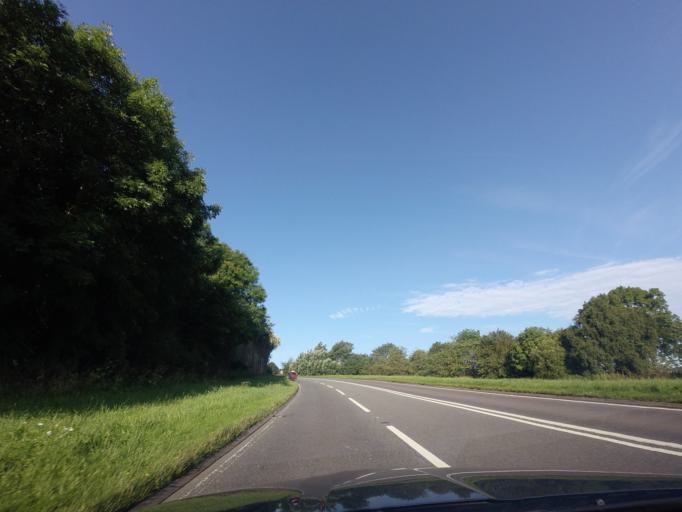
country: GB
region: England
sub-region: Derbyshire
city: Wingerworth
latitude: 53.2304
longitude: -1.5013
